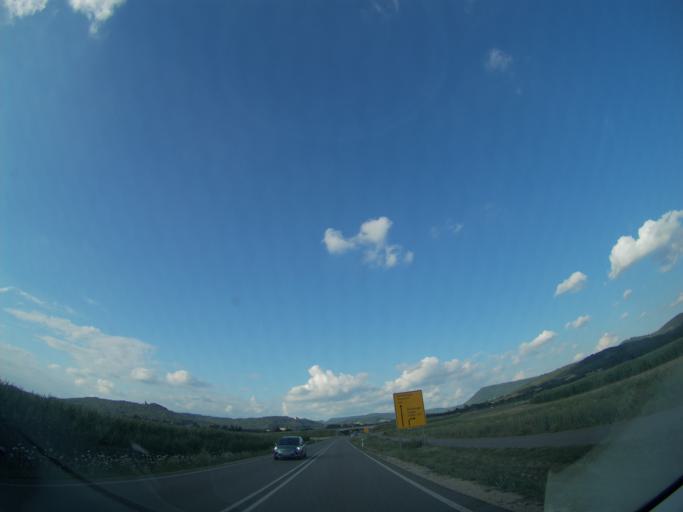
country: DE
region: Baden-Wuerttemberg
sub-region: Regierungsbezirk Stuttgart
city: Sussen
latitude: 48.6690
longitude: 9.7607
